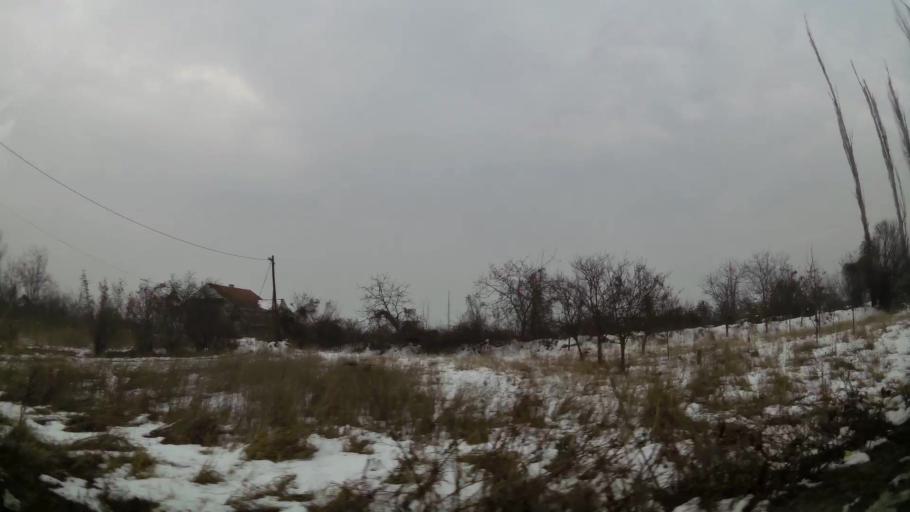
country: MK
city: Kondovo
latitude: 42.0529
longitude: 21.3484
